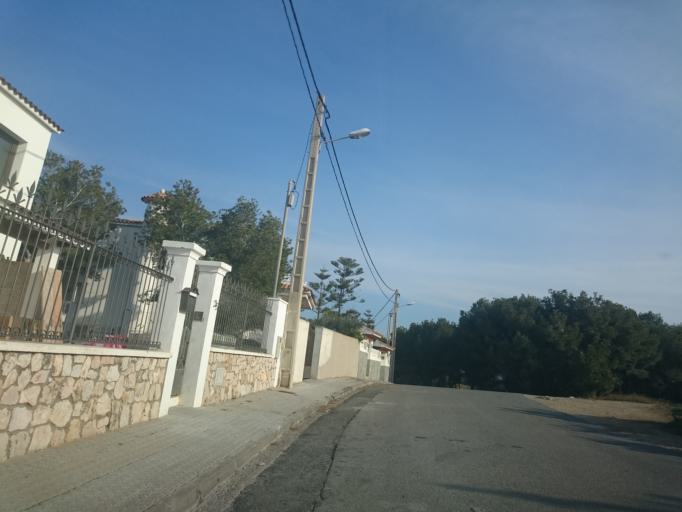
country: ES
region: Catalonia
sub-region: Provincia de Barcelona
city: Vilanova i la Geltru
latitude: 41.2272
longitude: 1.7572
